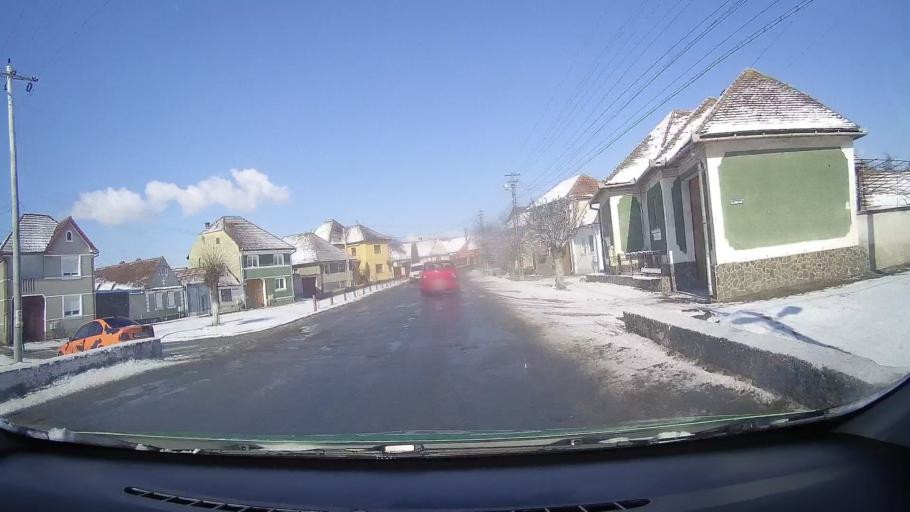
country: RO
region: Sibiu
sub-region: Comuna Avrig
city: Avrig
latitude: 45.7213
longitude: 24.3719
